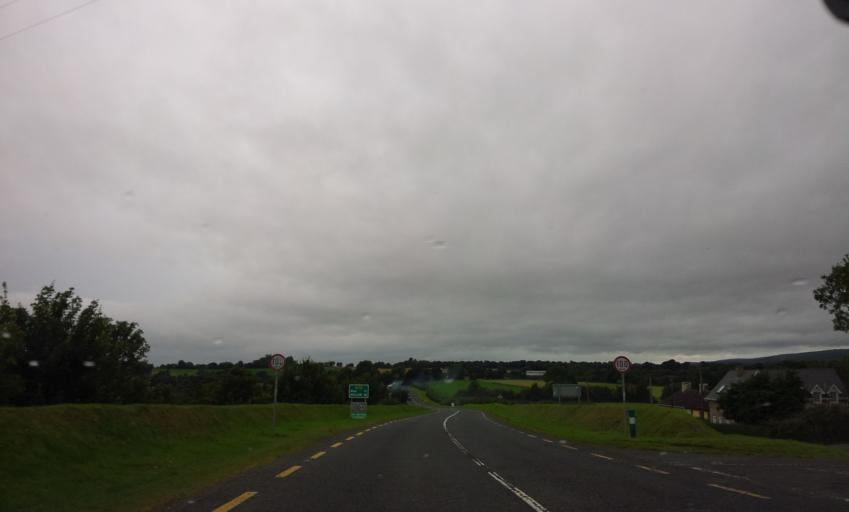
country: IE
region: Munster
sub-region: County Cork
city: Mitchelstown
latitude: 52.2451
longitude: -8.4353
